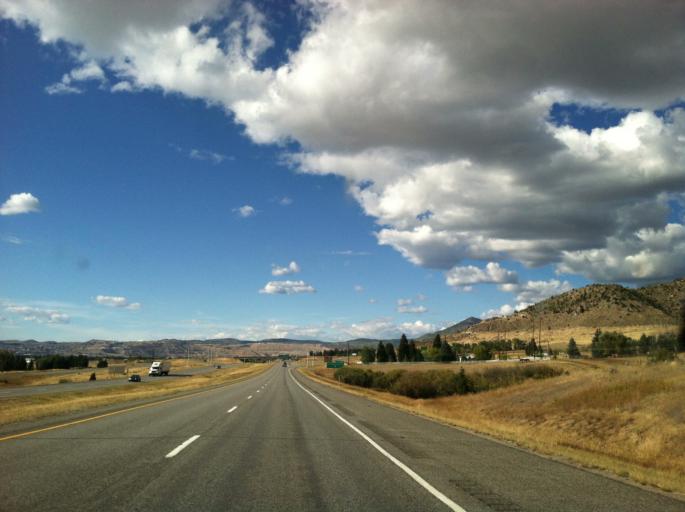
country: US
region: Montana
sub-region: Silver Bow County
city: Butte
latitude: 45.9551
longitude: -112.4689
